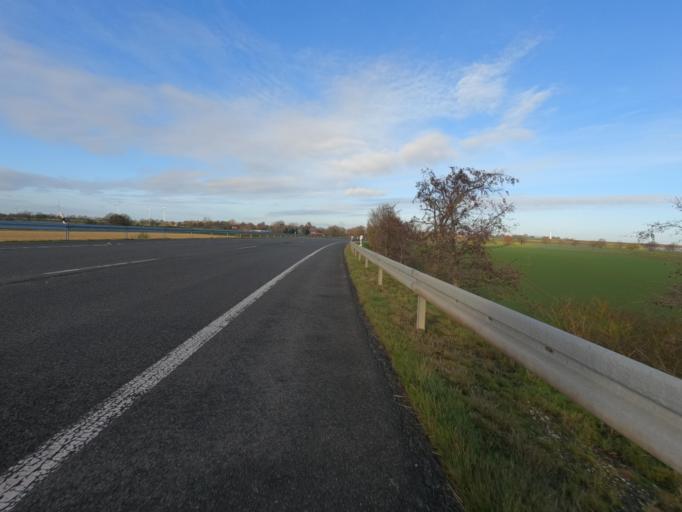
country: DE
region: North Rhine-Westphalia
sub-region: Regierungsbezirk Koln
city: Titz
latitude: 51.0040
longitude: 6.3944
